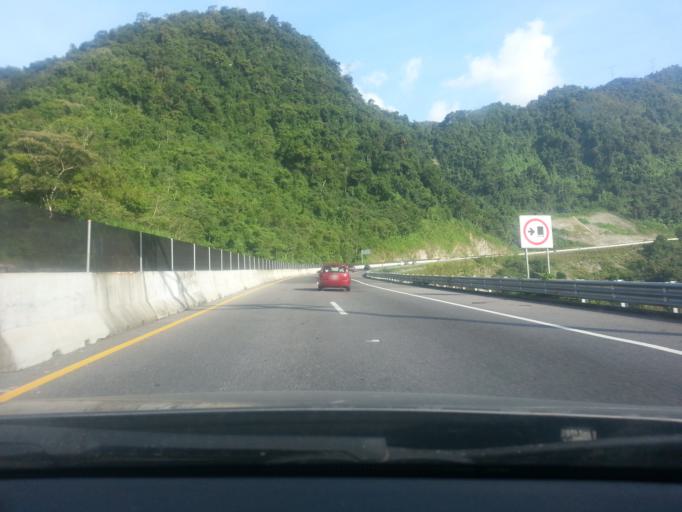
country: MX
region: Puebla
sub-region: Xicotepec
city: San Lorenzo
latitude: 20.3380
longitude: -97.9592
